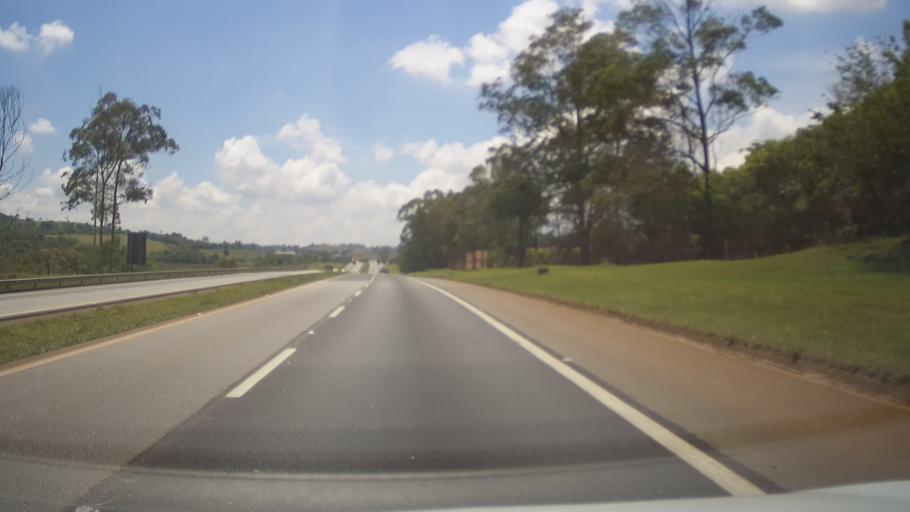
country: BR
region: Minas Gerais
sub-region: Sao Goncalo Do Sapucai
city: Sao Goncalo do Sapucai
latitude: -21.9190
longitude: -45.5963
